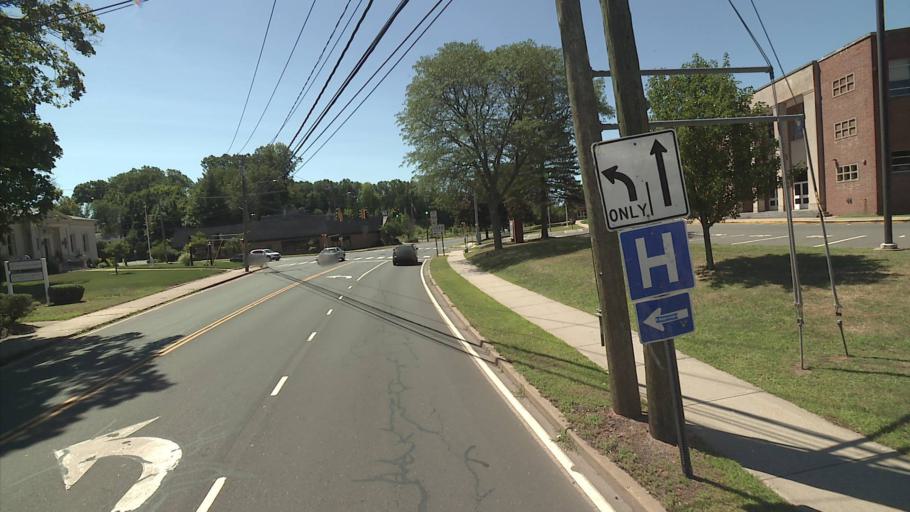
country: US
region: Connecticut
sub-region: Hartford County
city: Plainville
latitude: 41.5971
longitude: -72.8777
